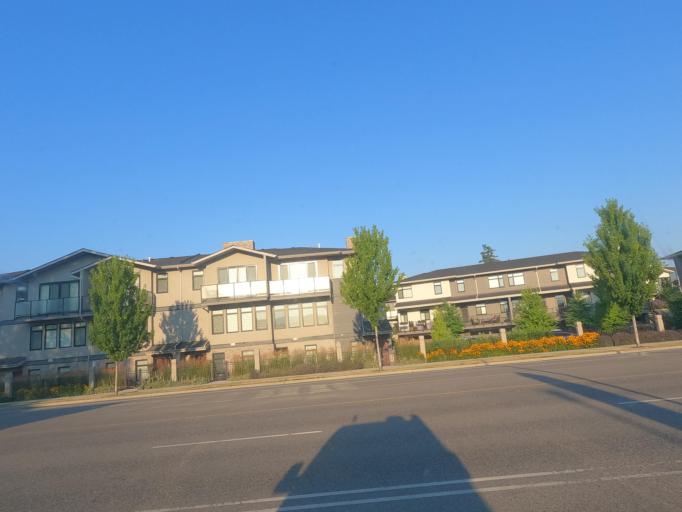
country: CA
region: British Columbia
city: Kelowna
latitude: 49.8713
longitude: -119.4752
